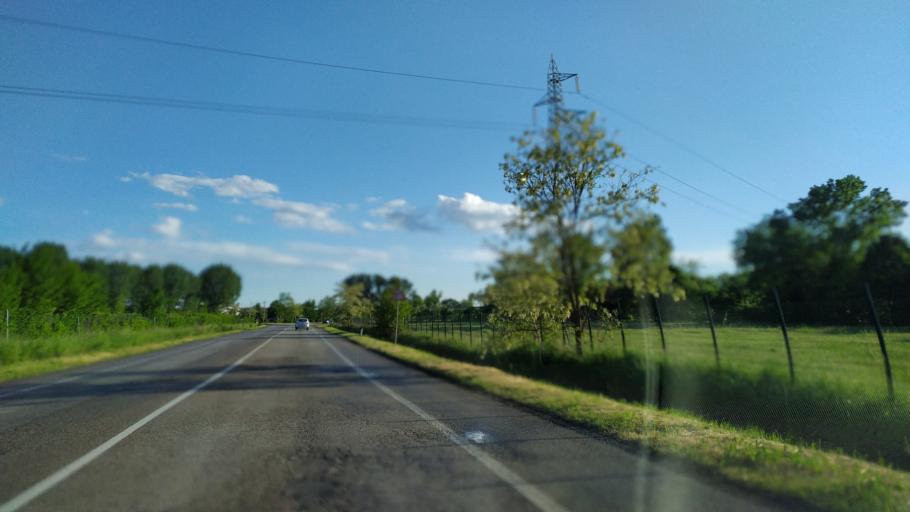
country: IT
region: Veneto
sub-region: Provincia di Padova
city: Taggi
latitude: 45.4533
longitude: 11.8345
